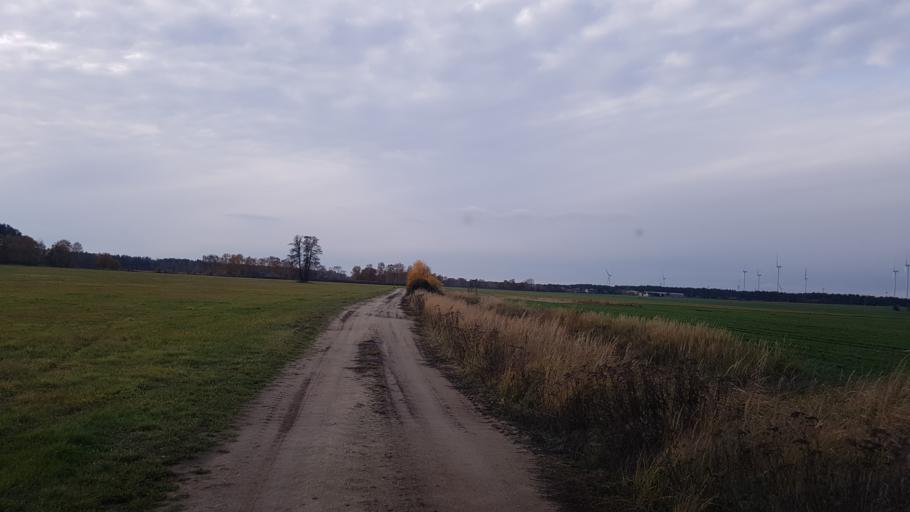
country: DE
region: Brandenburg
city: Trobitz
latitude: 51.6483
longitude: 13.4123
